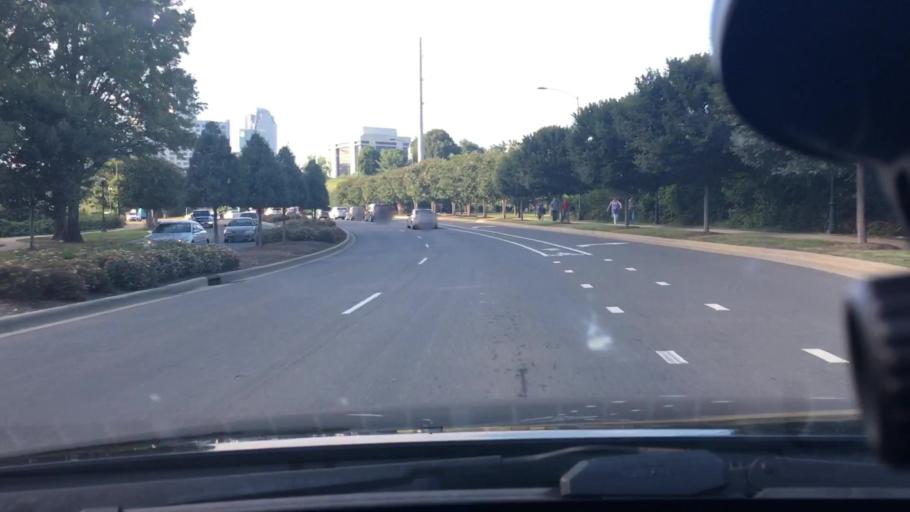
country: US
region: North Carolina
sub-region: Mecklenburg County
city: Charlotte
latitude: 35.2126
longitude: -80.8370
